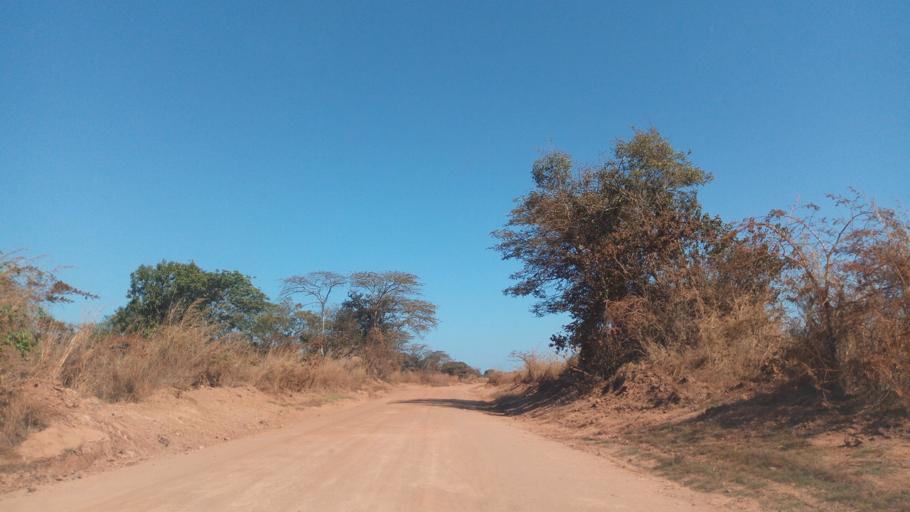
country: ZM
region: Luapula
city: Mwense
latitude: -10.7565
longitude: 28.2990
